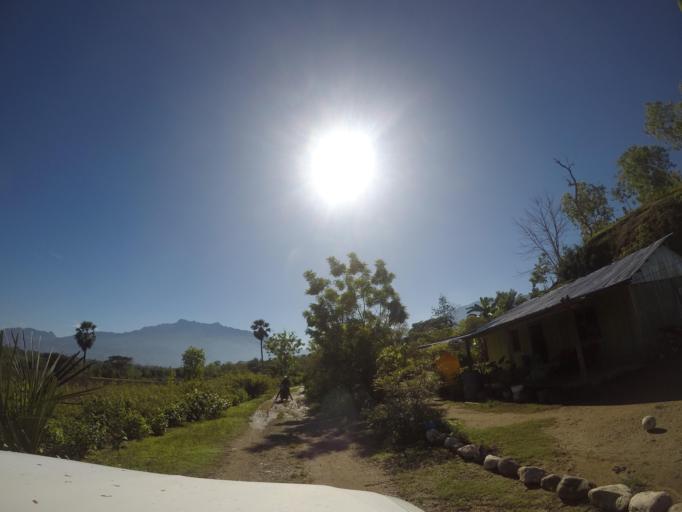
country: TL
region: Bobonaro
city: Maliana
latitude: -8.9985
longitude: 125.1955
